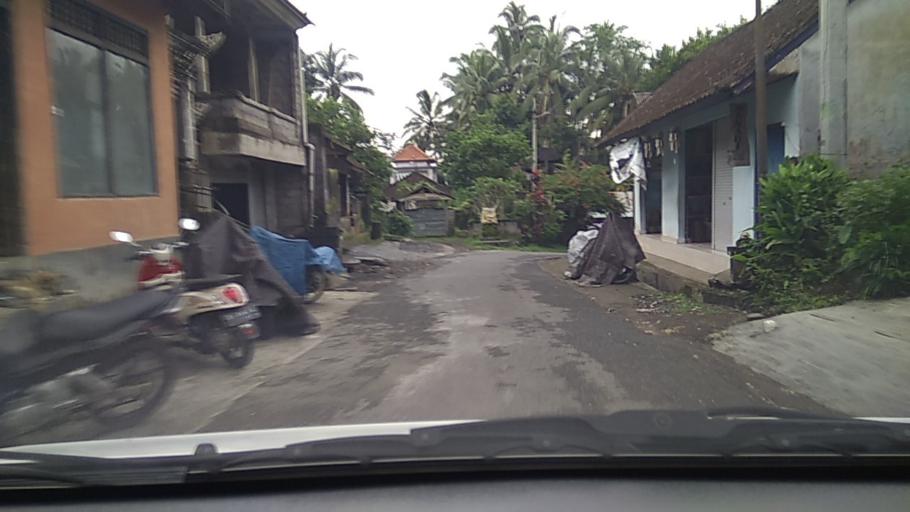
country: ID
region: Bali
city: Tegalalang
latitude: -8.4182
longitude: 115.2820
